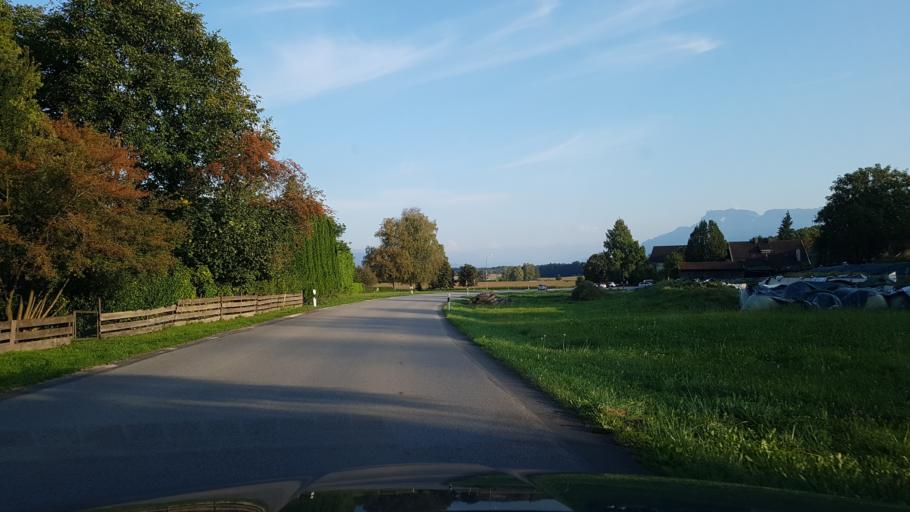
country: DE
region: Bavaria
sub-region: Upper Bavaria
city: Ainring
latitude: 47.8701
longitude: 12.9305
